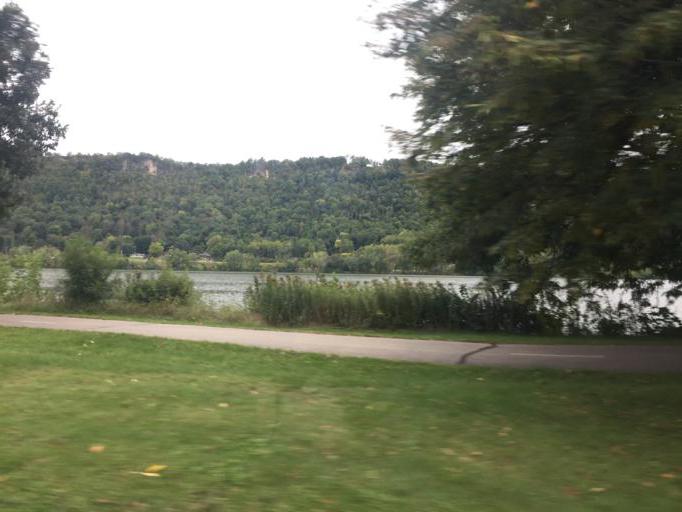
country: US
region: Minnesota
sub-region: Winona County
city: Winona
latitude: 44.0397
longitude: -91.6357
